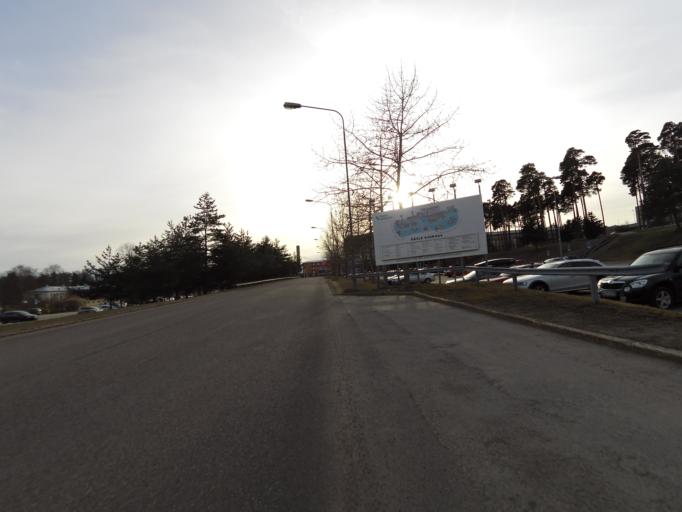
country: SE
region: Gaevleborg
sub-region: Gavle Kommun
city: Gavle
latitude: 60.6790
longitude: 17.1235
